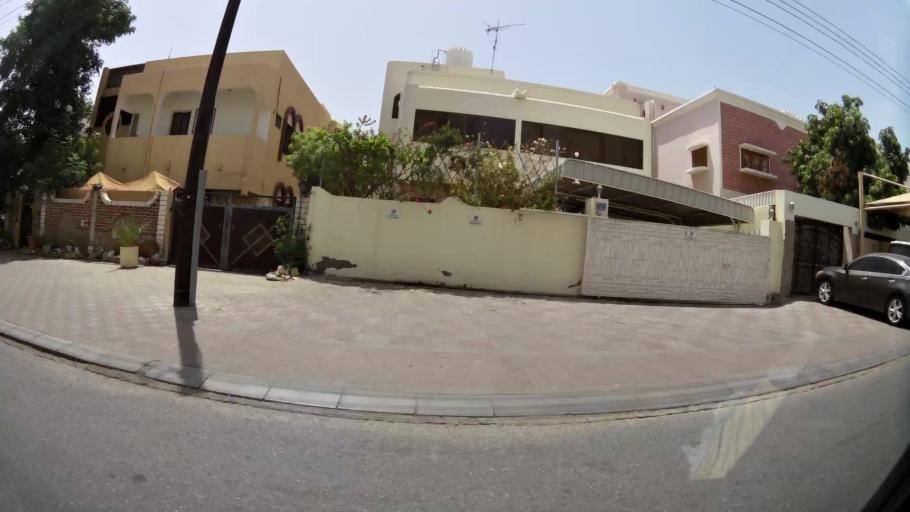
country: OM
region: Muhafazat Masqat
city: Bawshar
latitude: 23.5935
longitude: 58.4344
